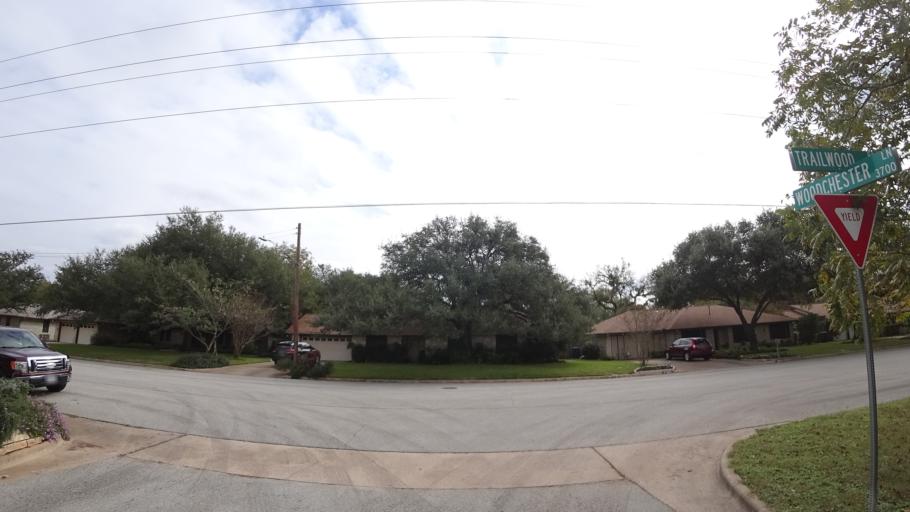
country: US
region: Texas
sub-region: Travis County
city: Wells Branch
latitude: 30.4287
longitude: -97.7082
